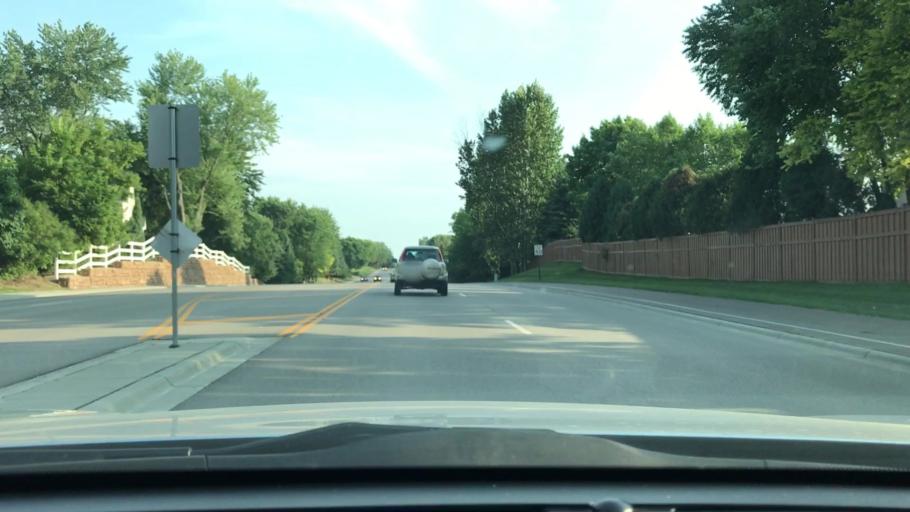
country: US
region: Minnesota
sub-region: Hennepin County
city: Maple Grove
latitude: 45.0429
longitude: -93.4818
